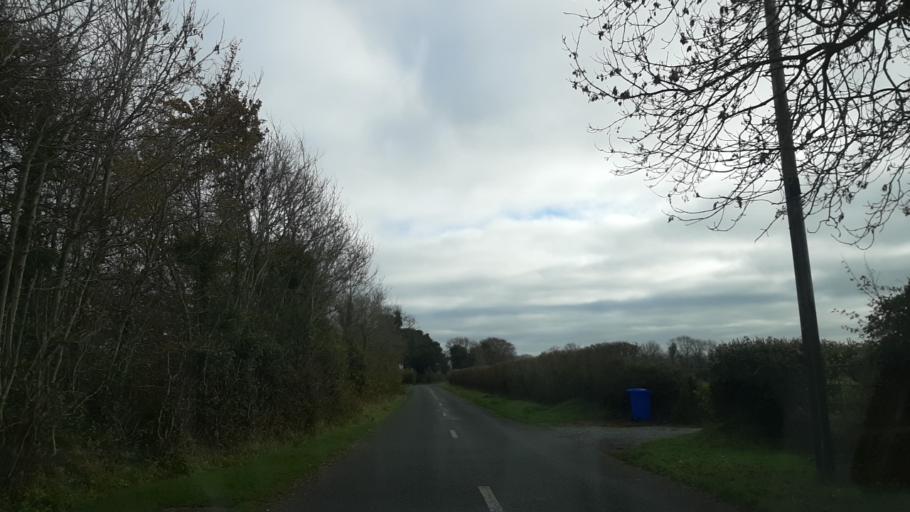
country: IE
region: Leinster
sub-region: Kildare
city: Kildare
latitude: 53.1817
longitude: -6.9112
